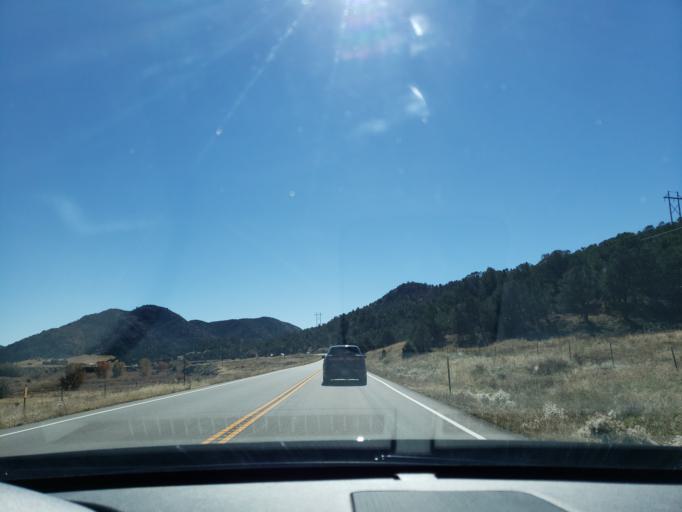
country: US
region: Colorado
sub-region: Fremont County
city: Canon City
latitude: 38.5938
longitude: -105.4249
